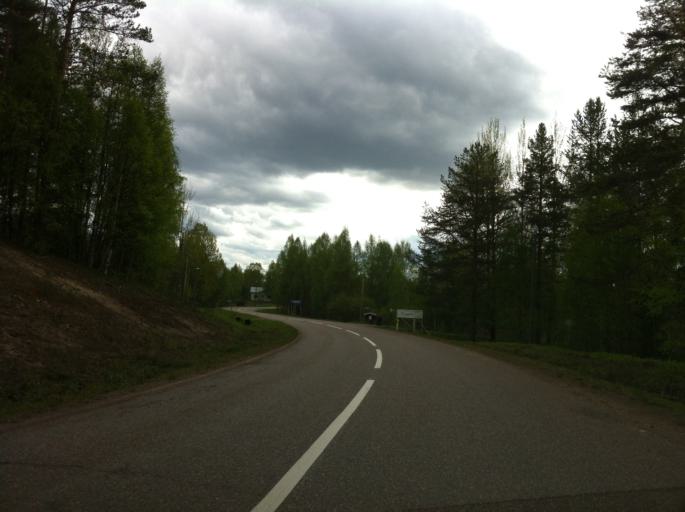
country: NO
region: Hedmark
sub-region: Trysil
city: Innbygda
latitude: 61.4222
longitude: 13.0867
